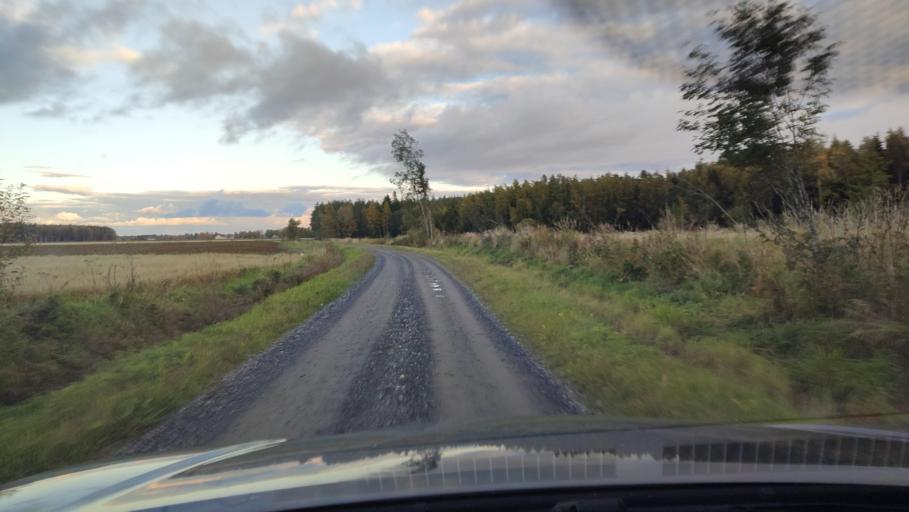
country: FI
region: Ostrobothnia
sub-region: Sydosterbotten
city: Kristinestad
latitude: 62.2512
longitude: 21.4587
